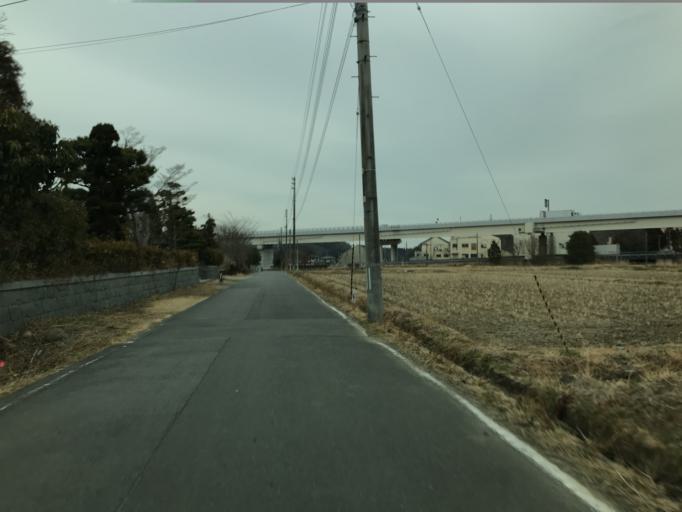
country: JP
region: Fukushima
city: Iwaki
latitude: 37.0690
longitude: 140.8372
